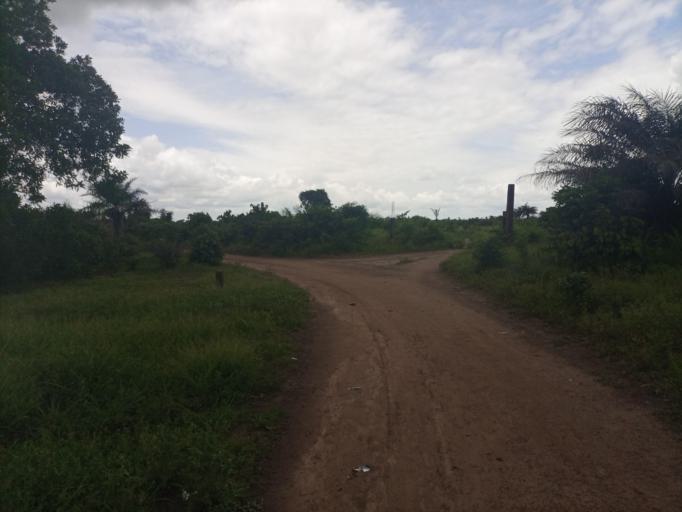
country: SL
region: Northern Province
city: Masoyila
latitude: 8.5777
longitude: -13.1577
